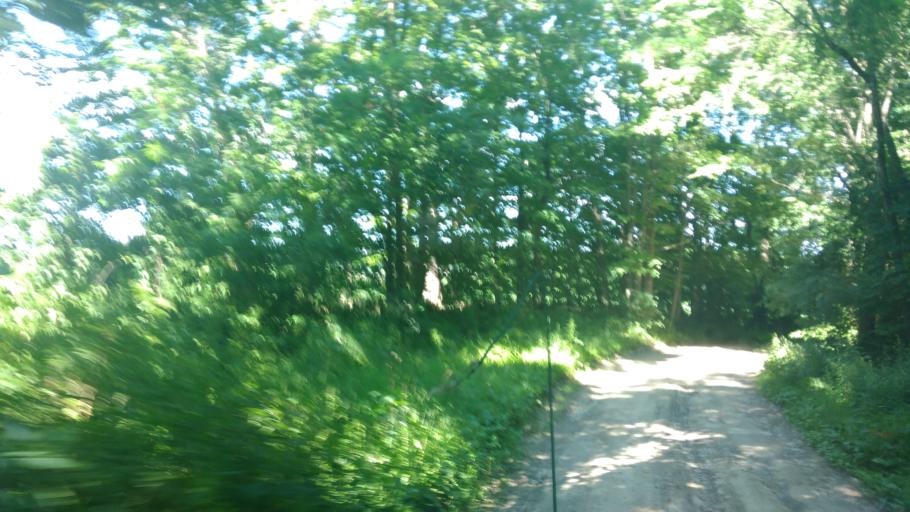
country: US
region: New York
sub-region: Wayne County
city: Clyde
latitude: 43.0268
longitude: -76.8684
